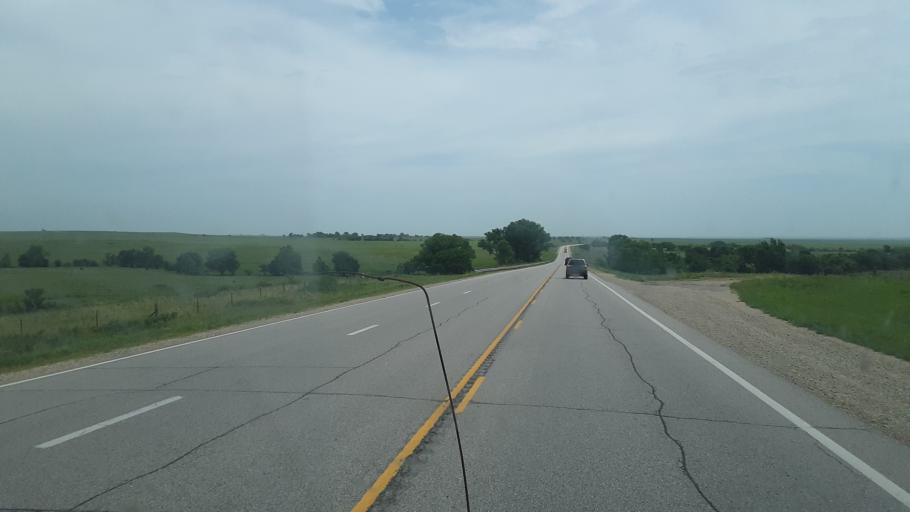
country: US
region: Kansas
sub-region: Greenwood County
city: Eureka
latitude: 37.8106
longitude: -96.5341
